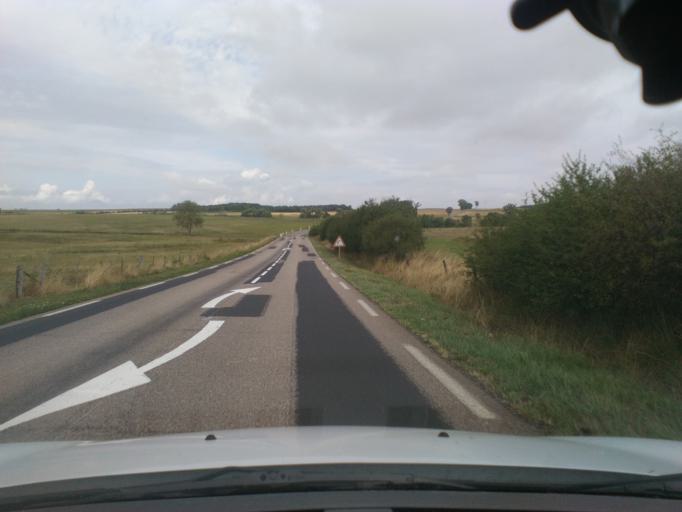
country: FR
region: Lorraine
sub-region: Departement de Meurthe-et-Moselle
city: Vezelise
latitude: 48.4283
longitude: 6.1255
